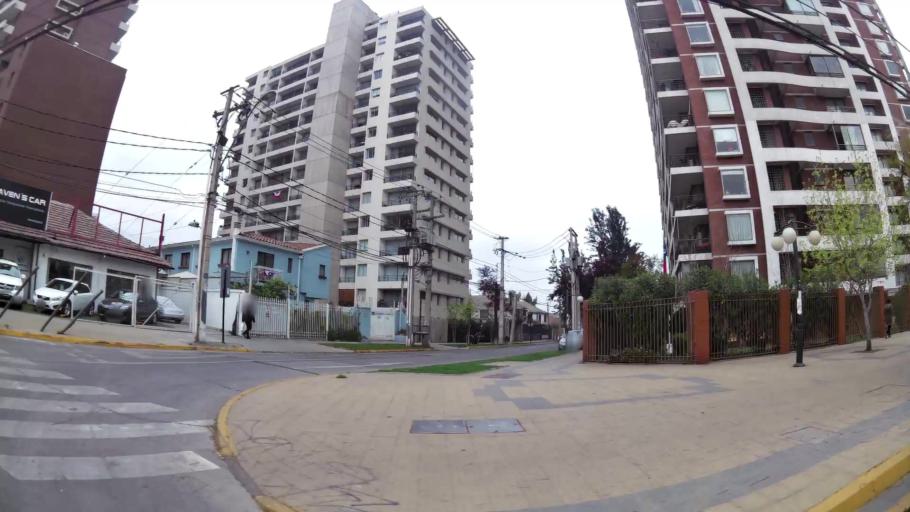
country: CL
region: Santiago Metropolitan
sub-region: Provincia de Santiago
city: Villa Presidente Frei, Nunoa, Santiago, Chile
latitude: -33.4553
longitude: -70.5846
